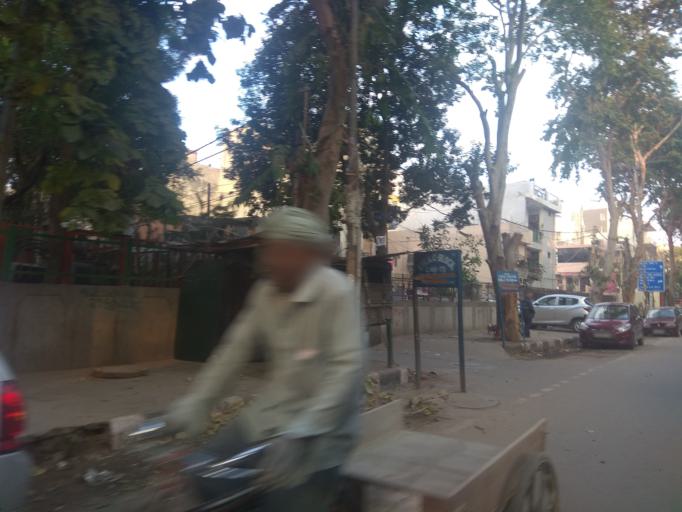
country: IN
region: NCT
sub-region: West Delhi
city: Nangloi Jat
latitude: 28.6317
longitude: 77.0704
